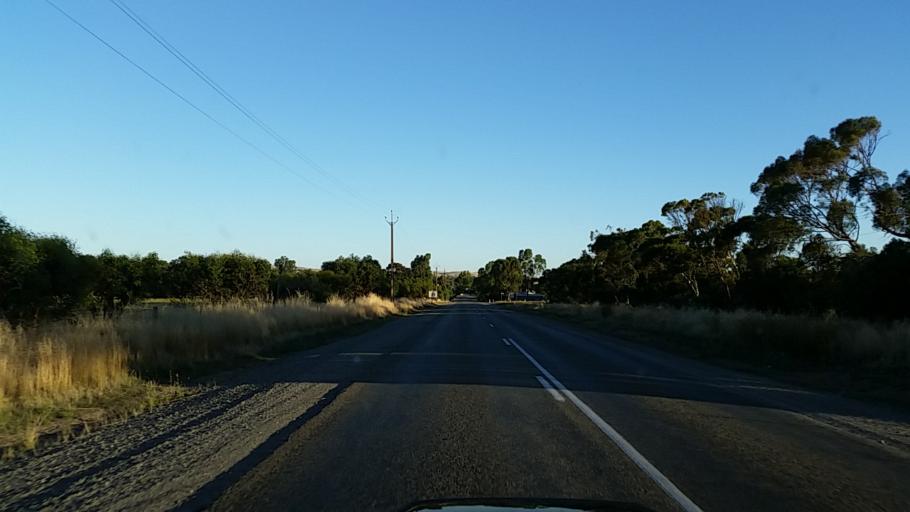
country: AU
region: South Australia
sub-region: Northern Areas
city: Jamestown
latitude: -33.4956
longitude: 138.6040
